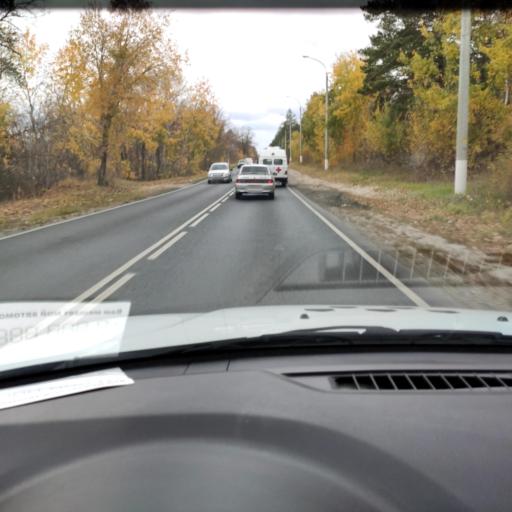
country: RU
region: Samara
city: Tol'yatti
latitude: 53.4735
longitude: 49.4020
